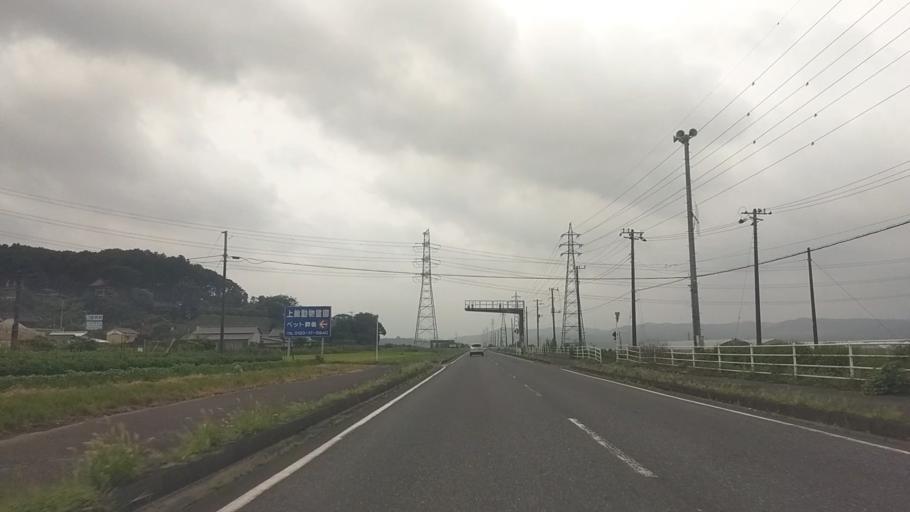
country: JP
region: Chiba
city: Kisarazu
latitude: 35.3461
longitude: 140.0548
